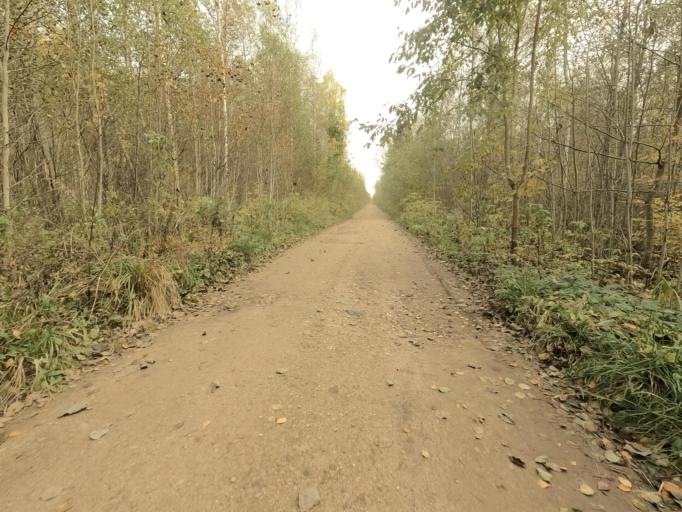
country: RU
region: Novgorod
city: Batetskiy
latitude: 58.8795
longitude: 30.7858
